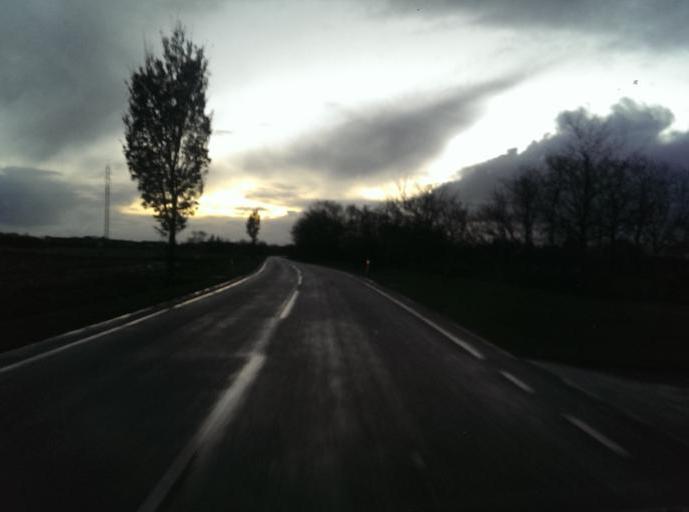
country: DK
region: South Denmark
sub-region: Esbjerg Kommune
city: Bramming
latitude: 55.4337
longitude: 8.6783
